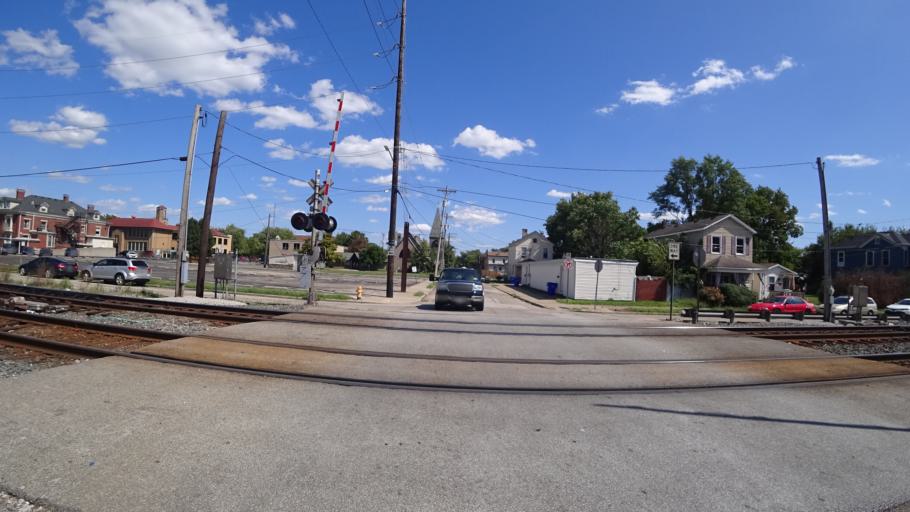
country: US
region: Ohio
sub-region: Butler County
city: Hamilton
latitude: 39.3997
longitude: -84.5569
